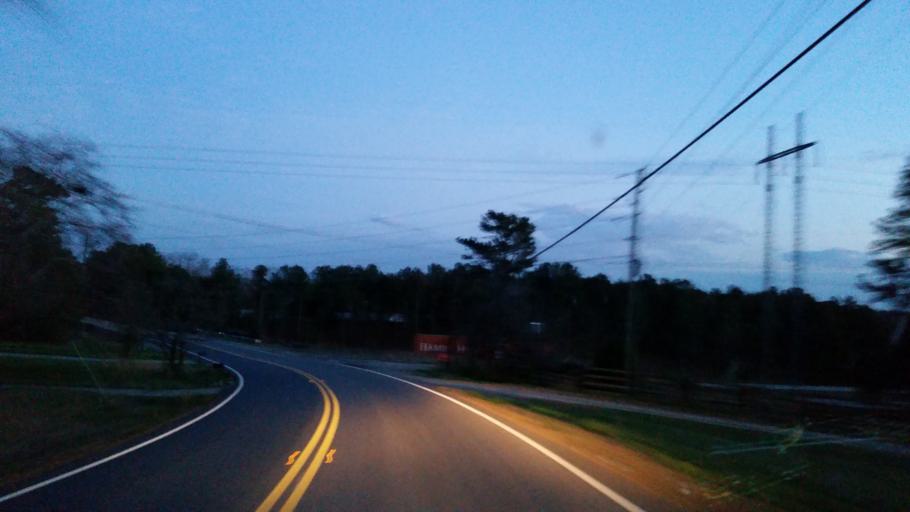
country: US
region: Georgia
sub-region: Cherokee County
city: Ball Ground
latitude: 34.2929
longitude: -84.4381
